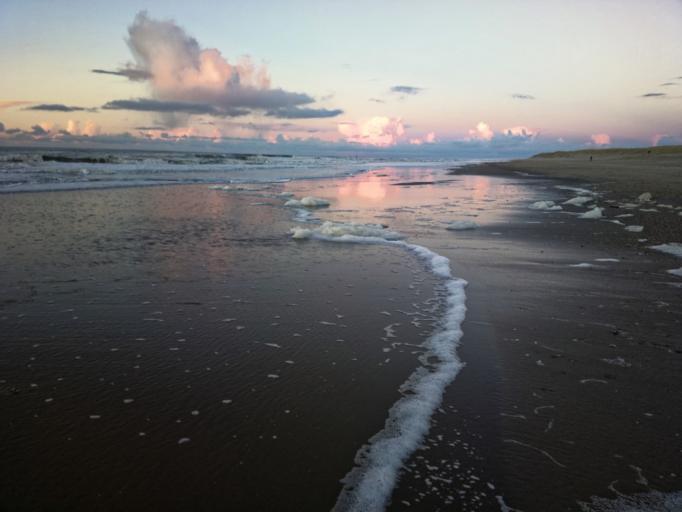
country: NL
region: North Holland
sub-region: Gemeente Texel
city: Den Burg
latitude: 53.0798
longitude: 4.7336
